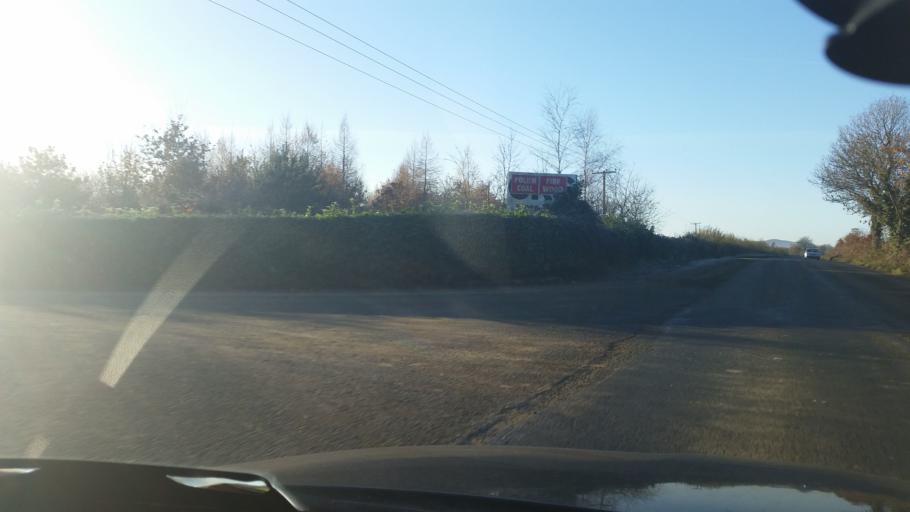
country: IE
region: Leinster
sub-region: Loch Garman
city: Gorey
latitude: 52.6411
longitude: -6.2950
